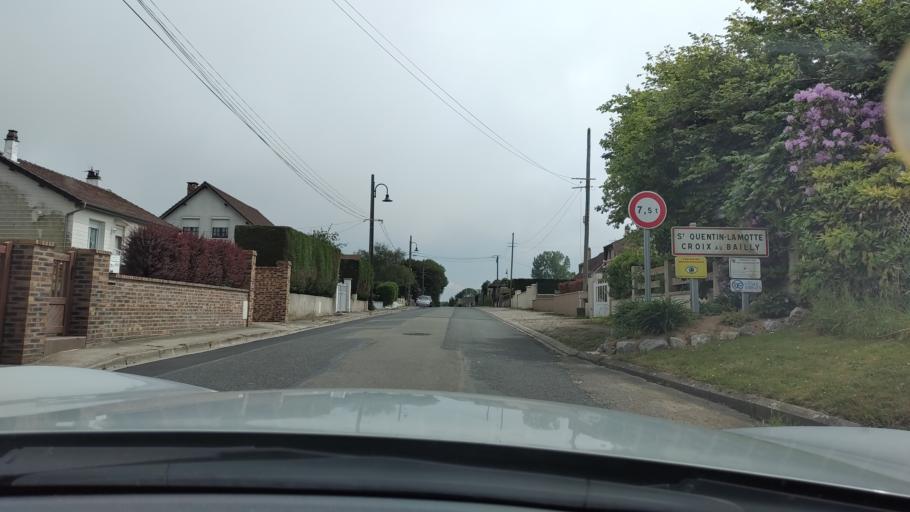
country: FR
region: Picardie
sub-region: Departement de la Somme
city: Ault
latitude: 50.0797
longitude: 1.4557
